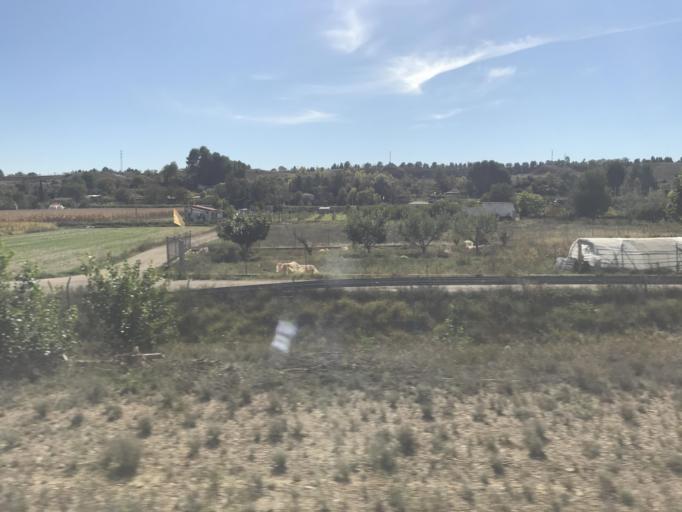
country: ES
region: Aragon
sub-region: Provincia de Zaragoza
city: Terrer
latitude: 41.3287
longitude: -1.6760
